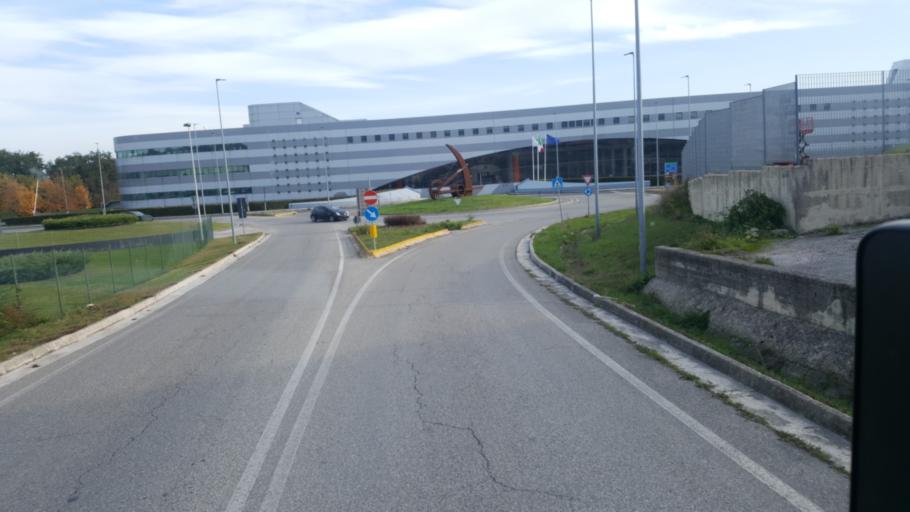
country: IT
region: The Marches
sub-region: Provincia di Pesaro e Urbino
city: Mondolfo
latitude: 43.7473
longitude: 13.1185
